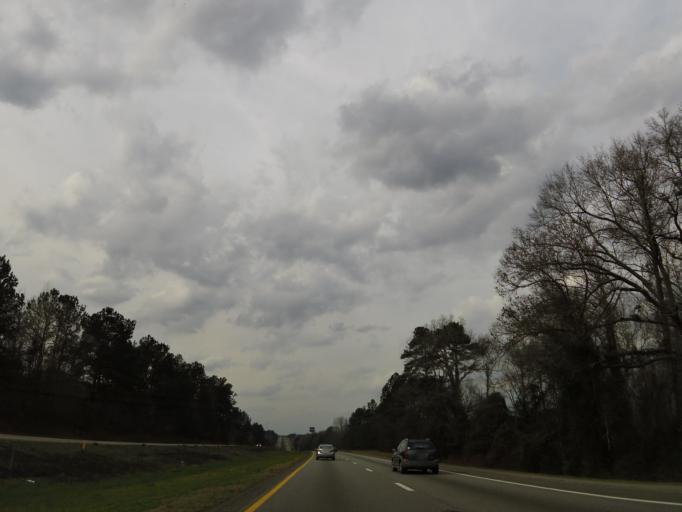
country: US
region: South Carolina
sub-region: Calhoun County
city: Saint Matthews
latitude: 33.6541
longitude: -80.8852
